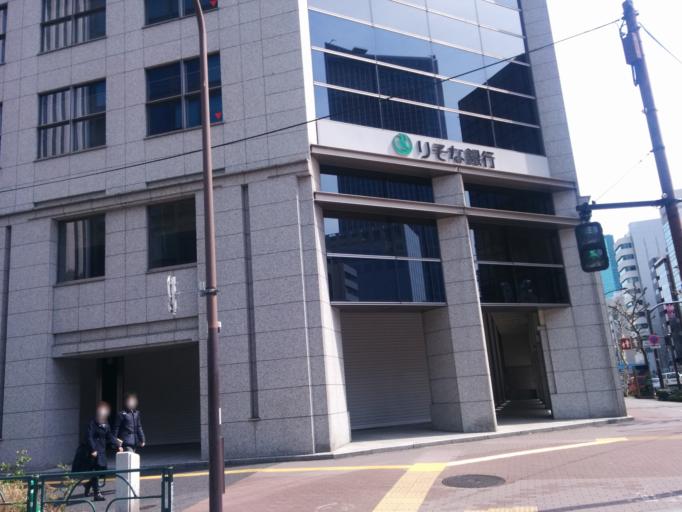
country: JP
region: Tokyo
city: Tokyo
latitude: 35.6698
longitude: 139.7517
